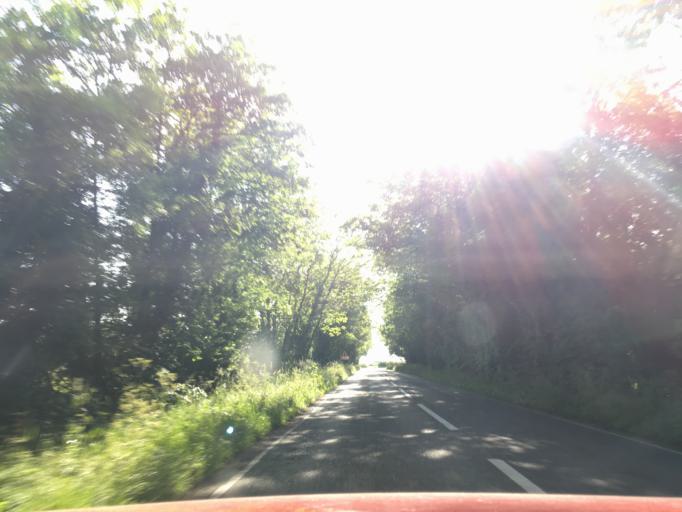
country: GB
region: England
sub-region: Oxfordshire
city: Stonesfield
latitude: 51.9260
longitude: -1.3990
